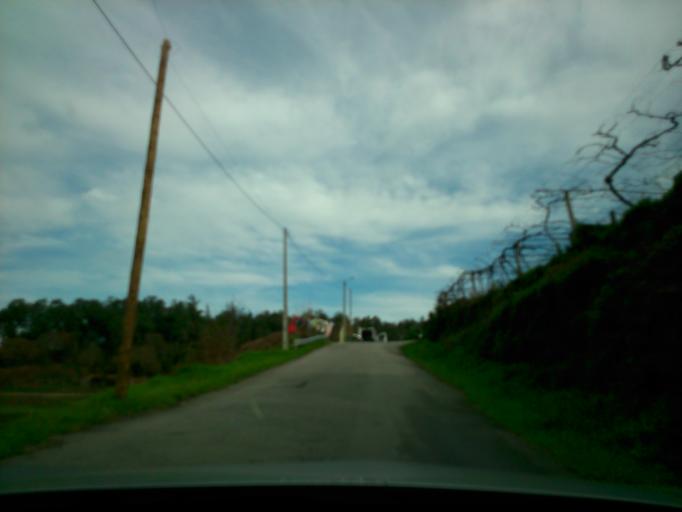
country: PT
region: Porto
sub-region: Amarante
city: Figueiro
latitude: 41.2932
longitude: -8.2017
